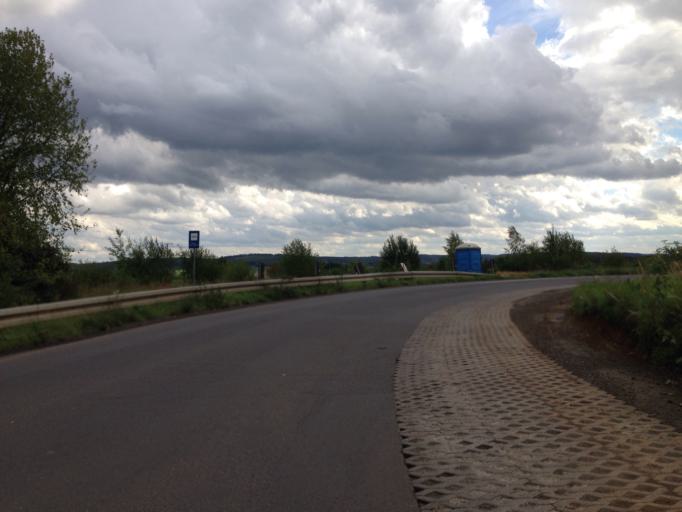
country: DE
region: Hesse
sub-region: Regierungsbezirk Giessen
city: Hungen
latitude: 50.4704
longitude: 8.9132
